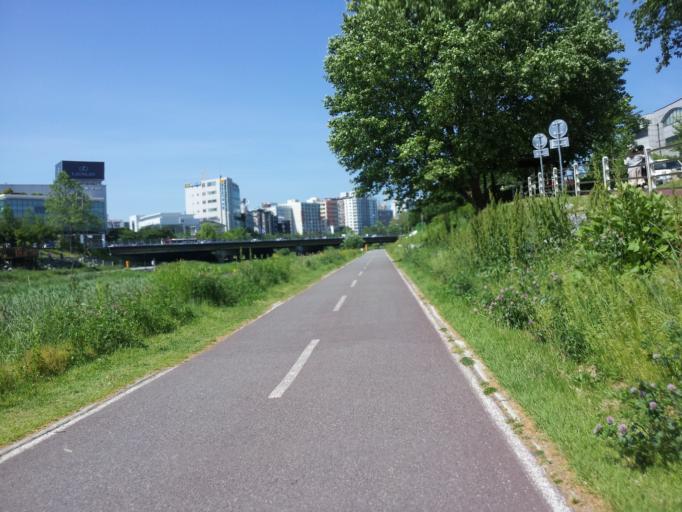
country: KR
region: Daejeon
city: Daejeon
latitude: 36.3608
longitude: 127.3552
